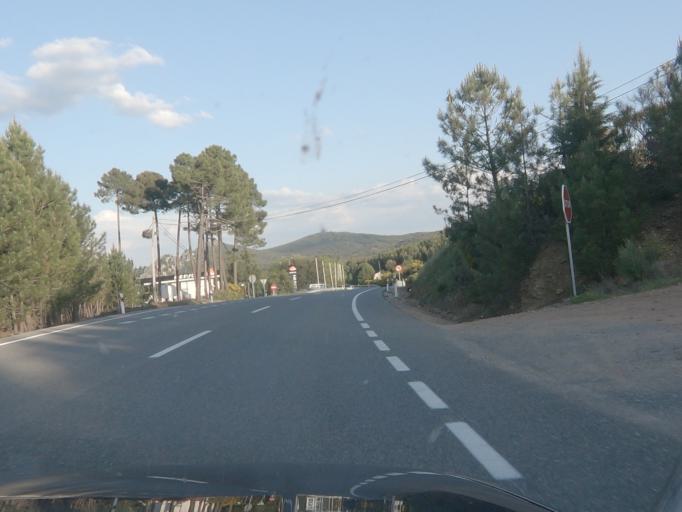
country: PT
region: Portalegre
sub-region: Portalegre
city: Sao Juliao
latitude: 39.3472
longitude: -7.2997
